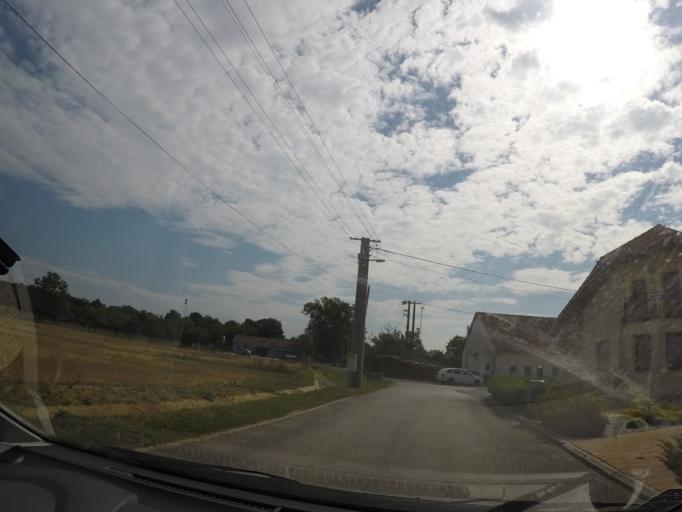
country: SK
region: Nitriansky
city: Levice
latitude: 48.2766
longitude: 18.6337
